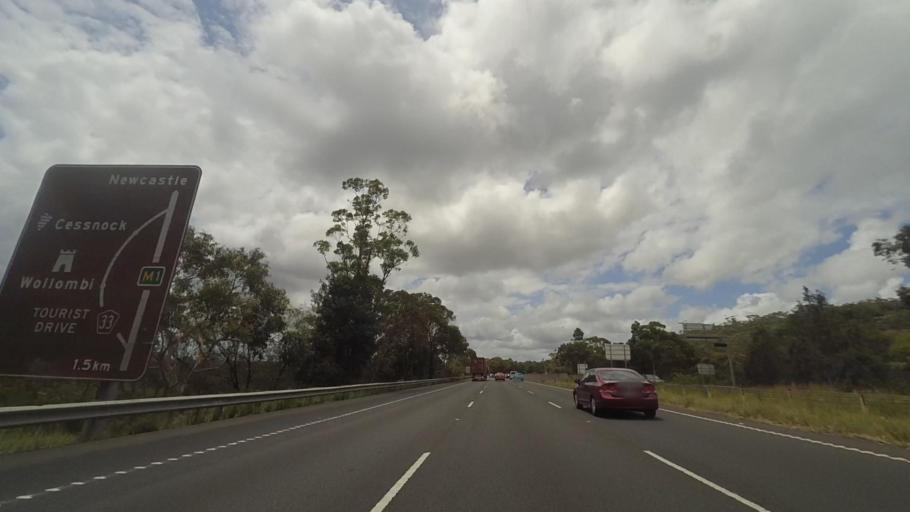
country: AU
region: New South Wales
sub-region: Gosford Shire
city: Point Clare
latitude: -33.4430
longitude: 151.2184
